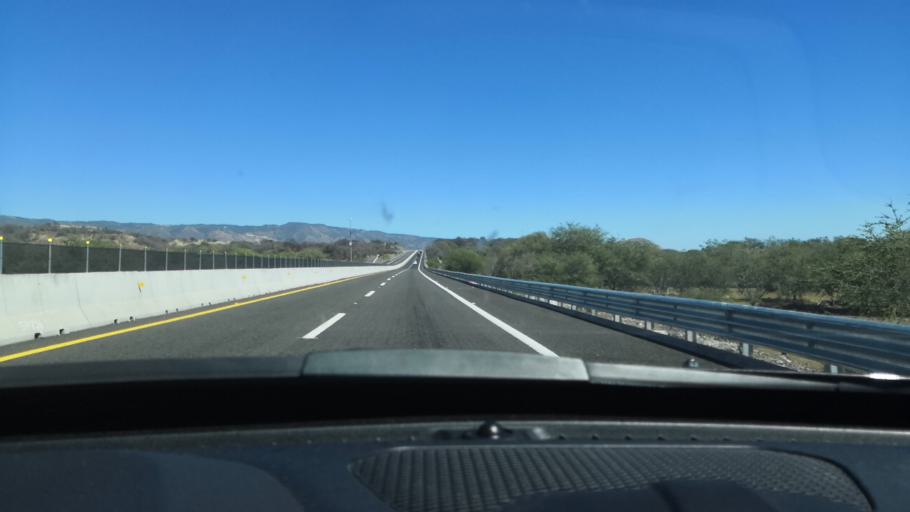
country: MX
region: Nayarit
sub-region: Ahuacatlan
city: Ahuacatlan
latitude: 21.0666
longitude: -104.4780
